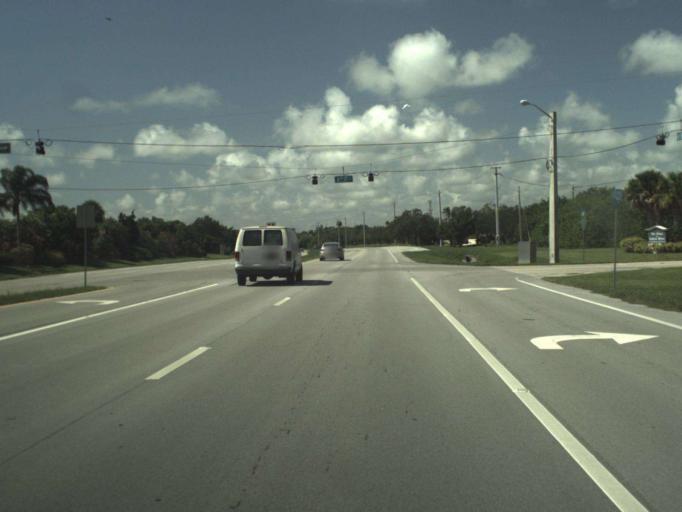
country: US
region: Florida
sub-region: Indian River County
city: Vero Beach
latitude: 27.6165
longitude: -80.3812
